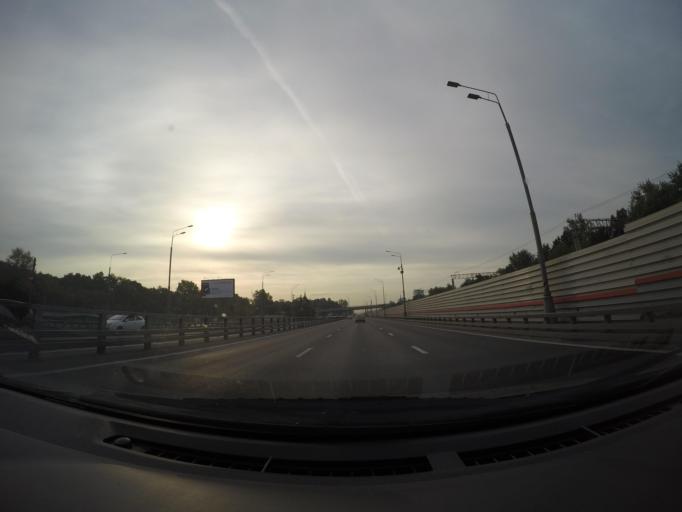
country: RU
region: Moscow
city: Perovo
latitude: 55.7250
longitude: 37.7922
